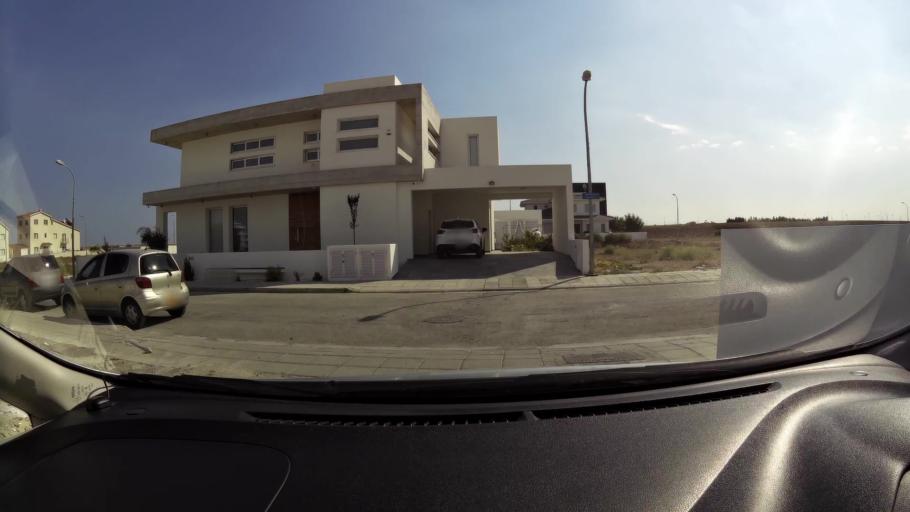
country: CY
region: Larnaka
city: Dhromolaxia
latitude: 34.9029
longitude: 33.5830
